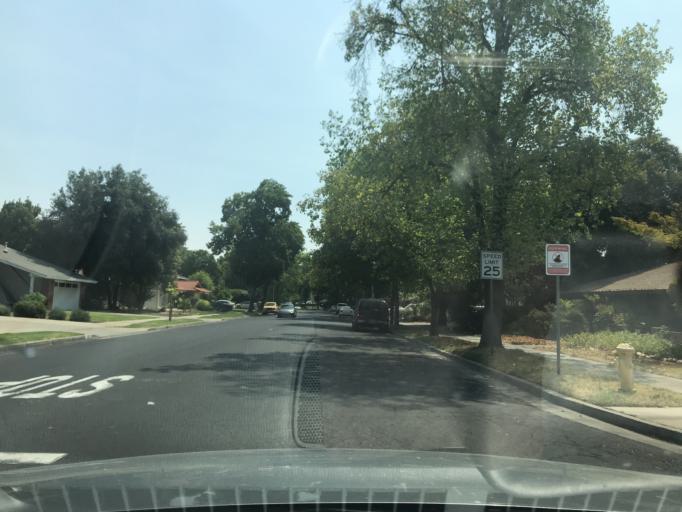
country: US
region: California
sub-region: Merced County
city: Merced
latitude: 37.3153
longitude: -120.4785
